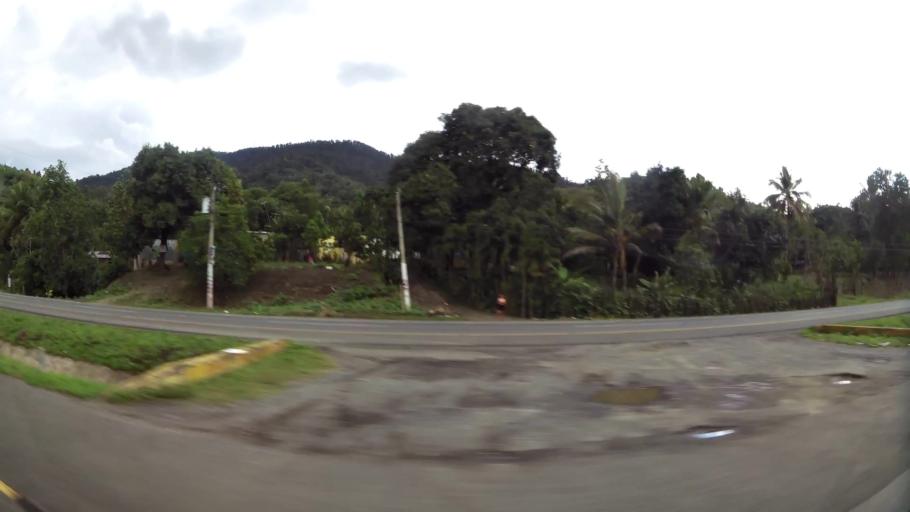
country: DO
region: San Cristobal
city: Villa Altagracia
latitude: 18.6962
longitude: -70.1881
